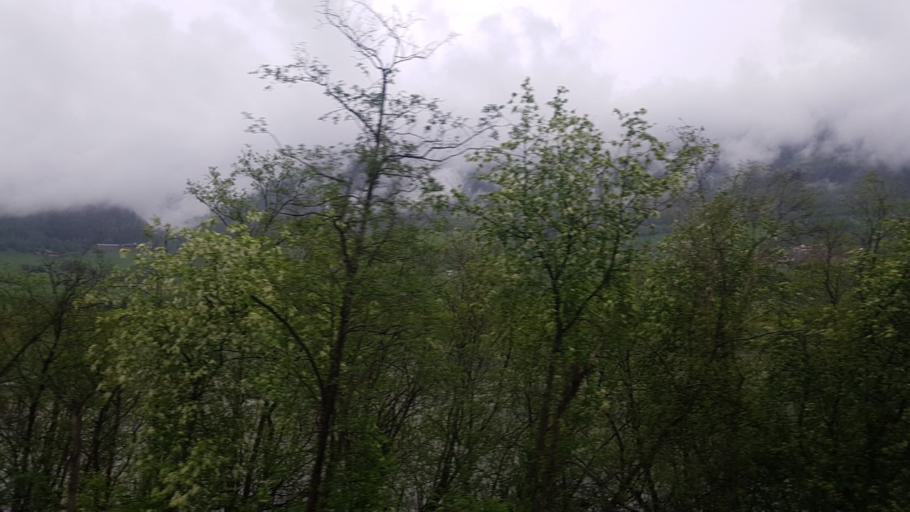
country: NO
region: Oppland
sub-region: Oyer
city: Tretten
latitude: 61.3883
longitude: 10.2540
